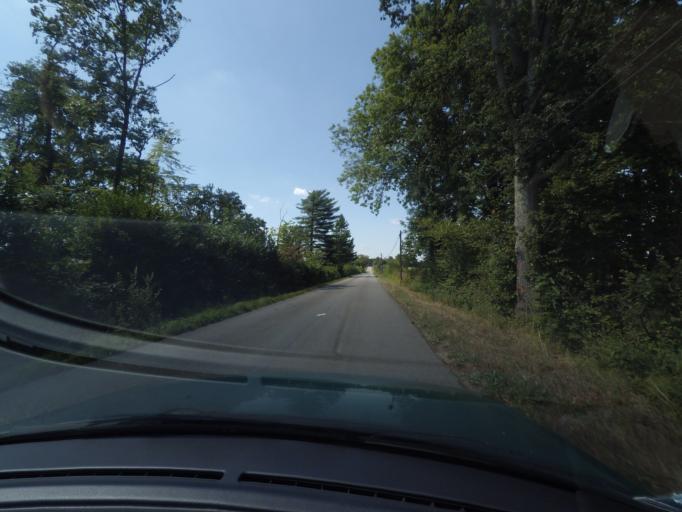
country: FR
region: Limousin
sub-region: Departement de la Haute-Vienne
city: Aixe-sur-Vienne
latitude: 45.7833
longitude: 1.1606
